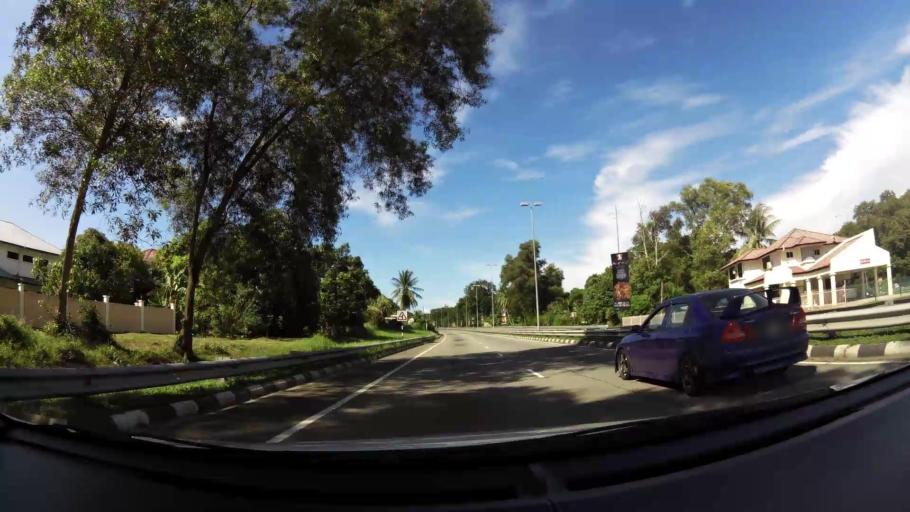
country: BN
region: Brunei and Muara
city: Bandar Seri Begawan
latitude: 4.9548
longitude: 114.9474
